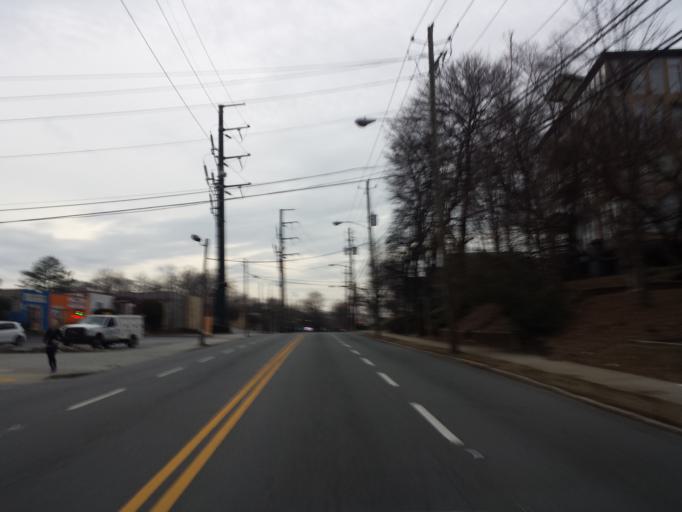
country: US
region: Georgia
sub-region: Fulton County
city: Atlanta
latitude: 33.7862
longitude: -84.3962
